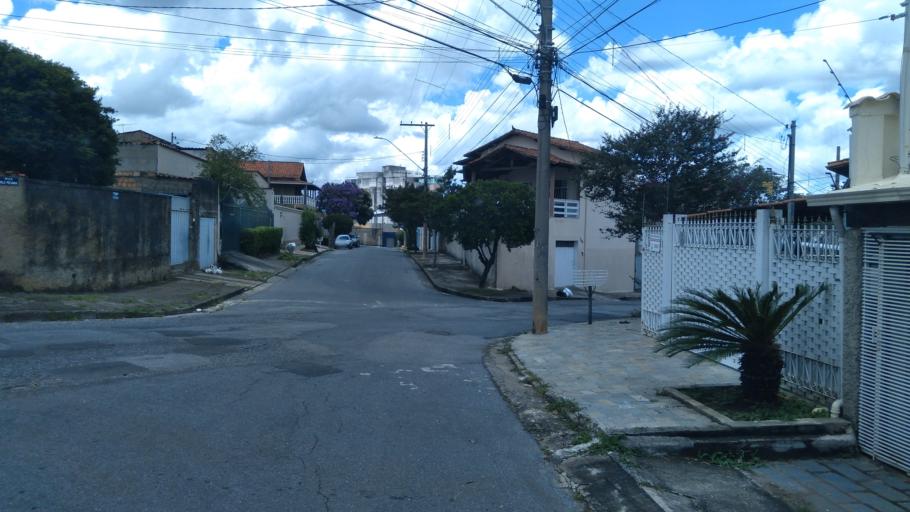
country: BR
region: Minas Gerais
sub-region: Belo Horizonte
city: Belo Horizonte
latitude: -19.8930
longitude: -43.9069
